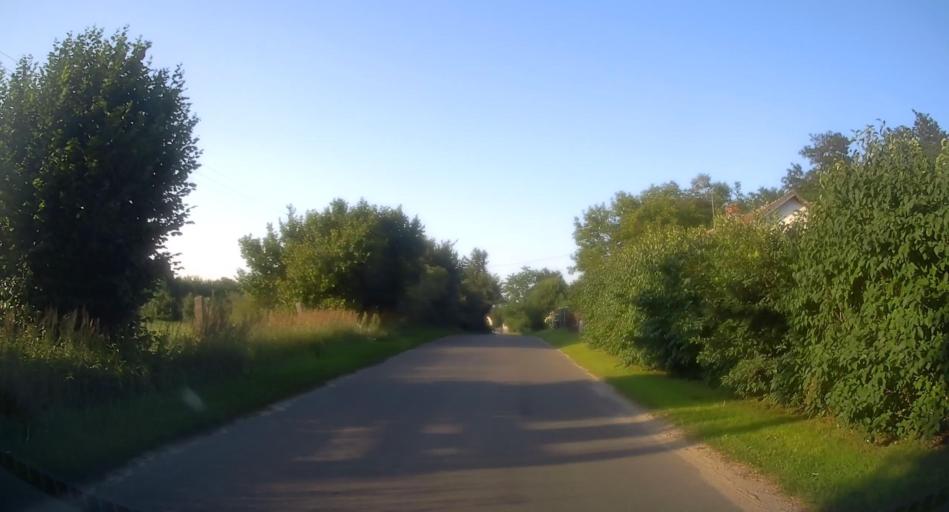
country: PL
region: Lodz Voivodeship
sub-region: Powiat skierniewicki
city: Kaweczyn Nowy
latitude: 51.8995
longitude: 20.3042
